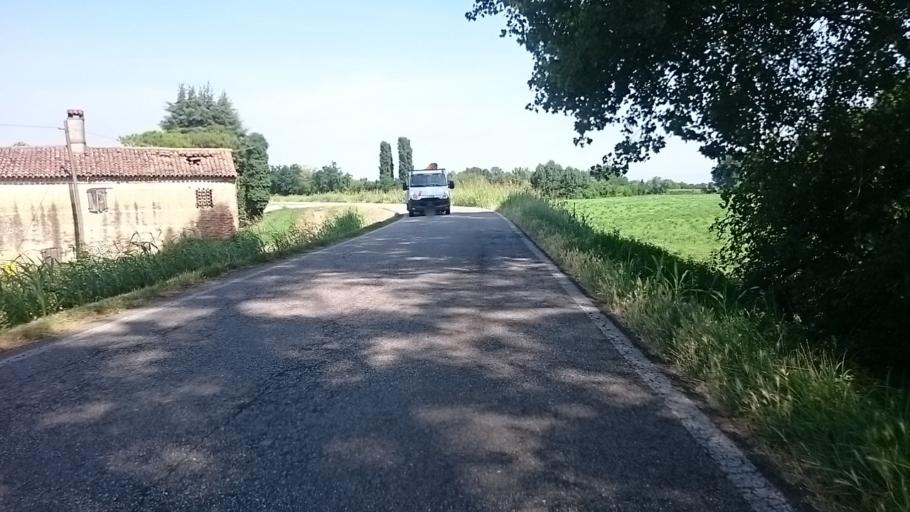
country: IT
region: Veneto
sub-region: Provincia di Padova
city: Cervarese Santa Croce
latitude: 45.4155
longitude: 11.7094
